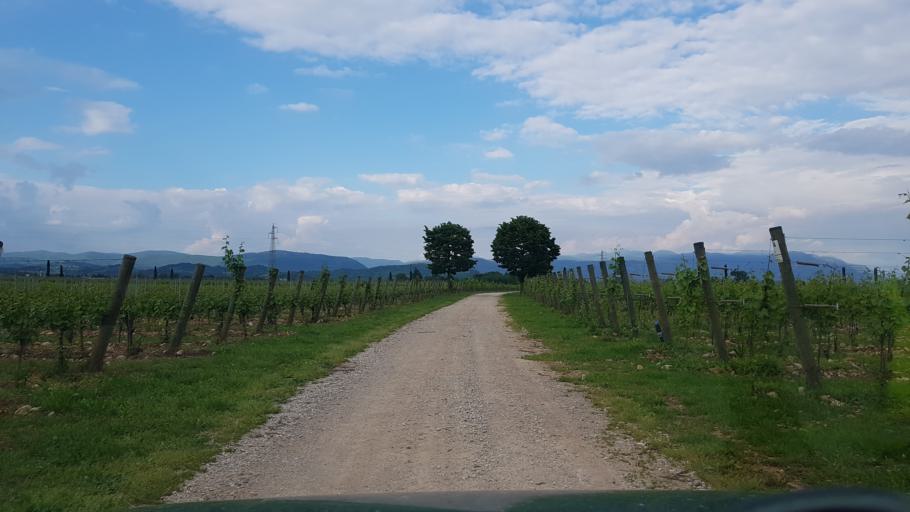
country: IT
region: Friuli Venezia Giulia
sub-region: Provincia di Gorizia
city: San Lorenzo Isontino
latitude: 45.9181
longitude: 13.5331
